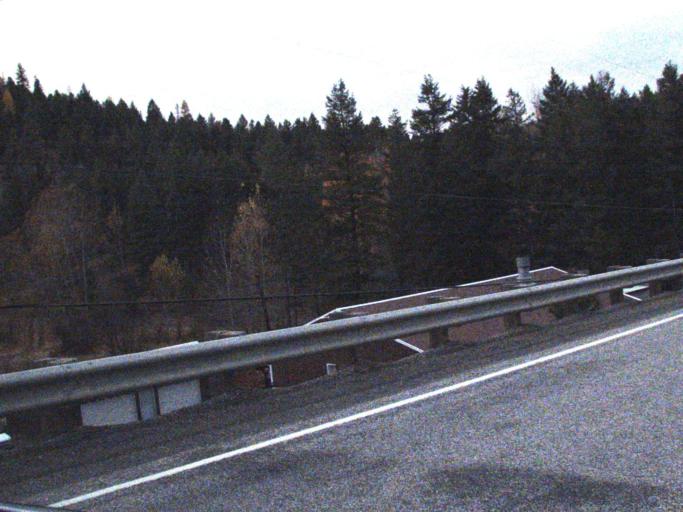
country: US
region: Washington
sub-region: Ferry County
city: Republic
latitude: 48.6440
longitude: -118.6847
